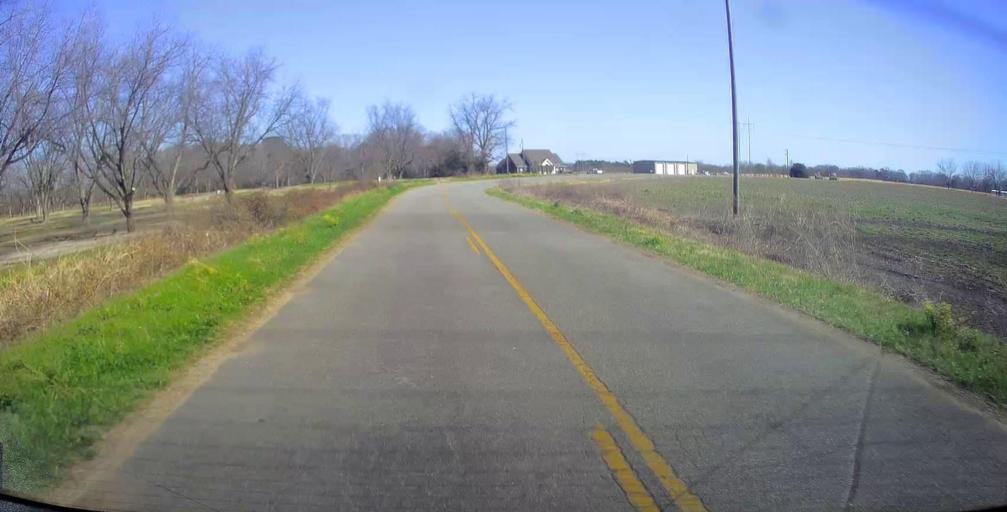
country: US
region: Georgia
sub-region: Peach County
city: Byron
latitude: 32.6293
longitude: -83.8413
